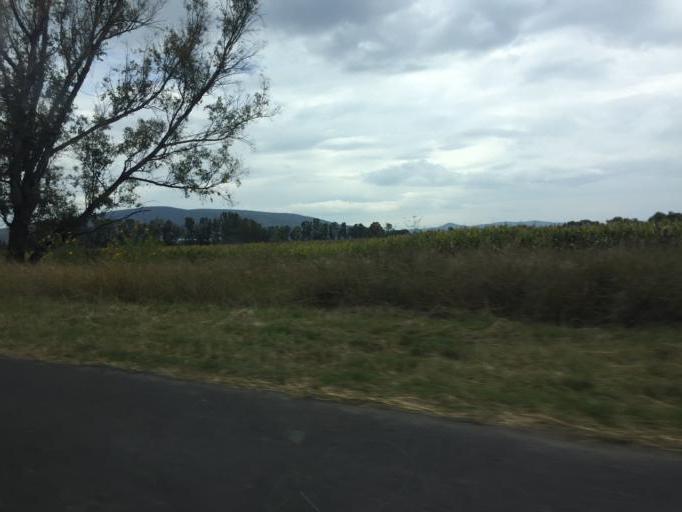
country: MX
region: Jalisco
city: Ocotlan
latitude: 20.3882
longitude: -102.7131
